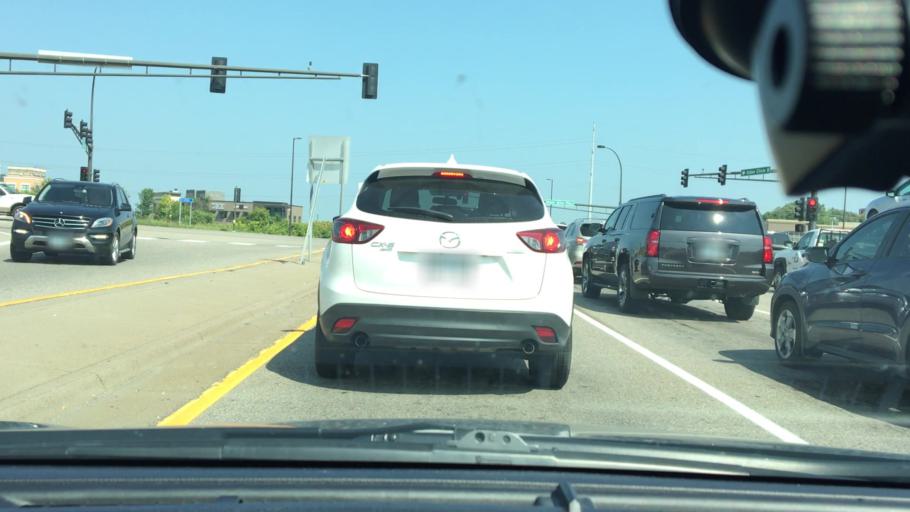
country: US
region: Minnesota
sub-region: Hennepin County
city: Maple Grove
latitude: 45.1280
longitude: -93.4829
